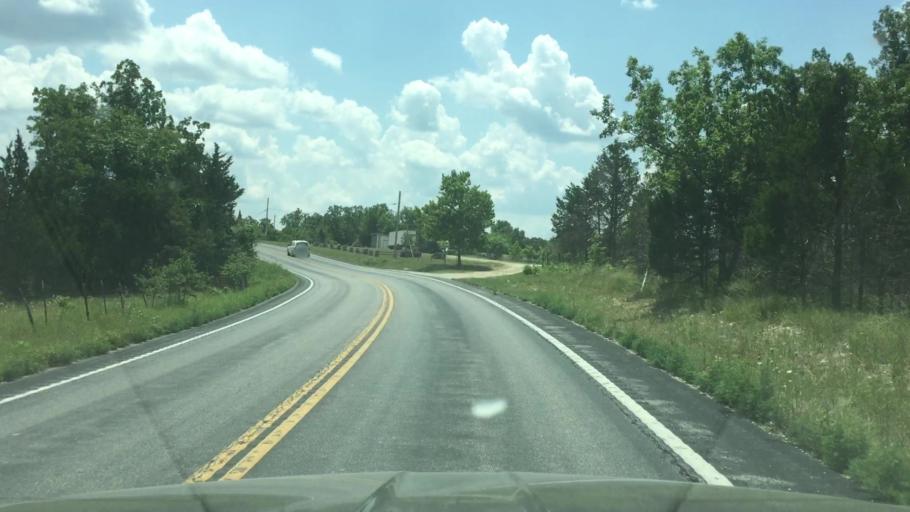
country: US
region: Missouri
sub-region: Miller County
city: Tuscumbia
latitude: 38.1067
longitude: -92.5014
